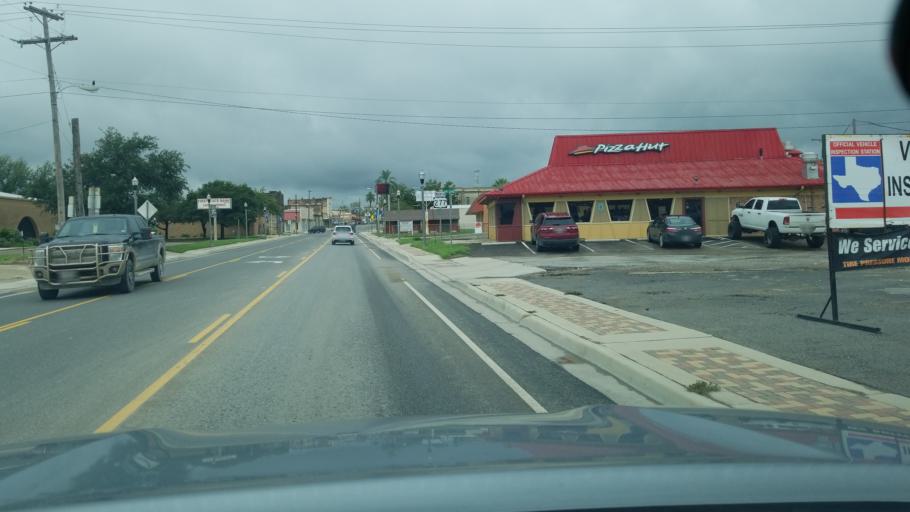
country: US
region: Texas
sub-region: Dimmit County
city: Carrizo Springs
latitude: 28.5213
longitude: -99.8579
